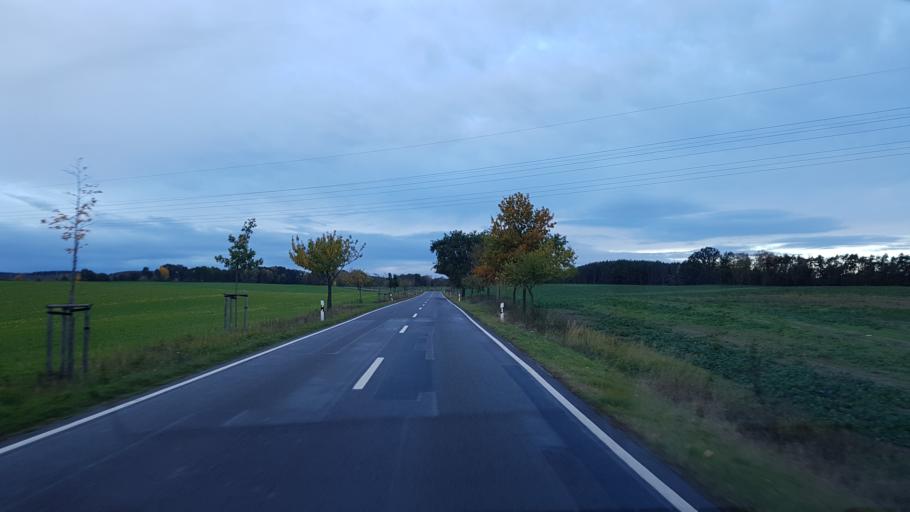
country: DE
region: Saxony
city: Belgern
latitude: 51.4444
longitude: 13.1014
